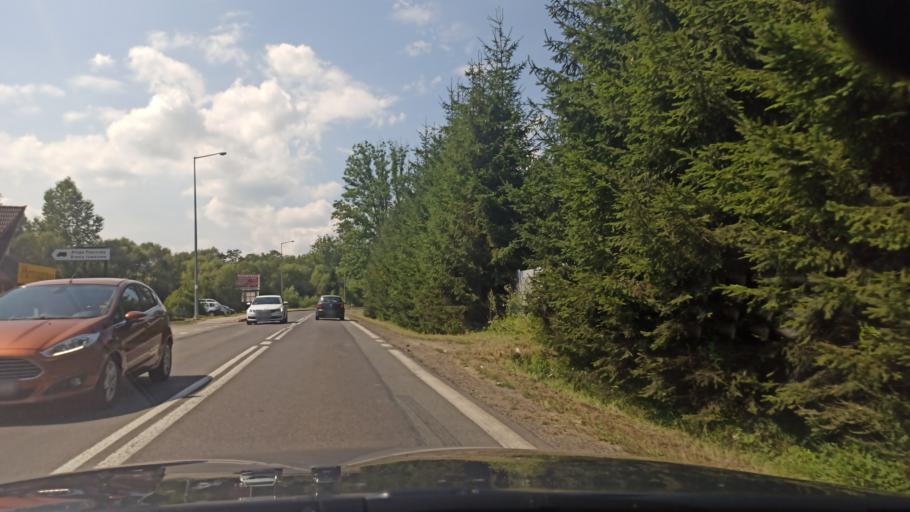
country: PL
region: Lesser Poland Voivodeship
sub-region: Powiat nowotarski
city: Kroscienko nad Dunajcem
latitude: 49.4387
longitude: 20.4043
